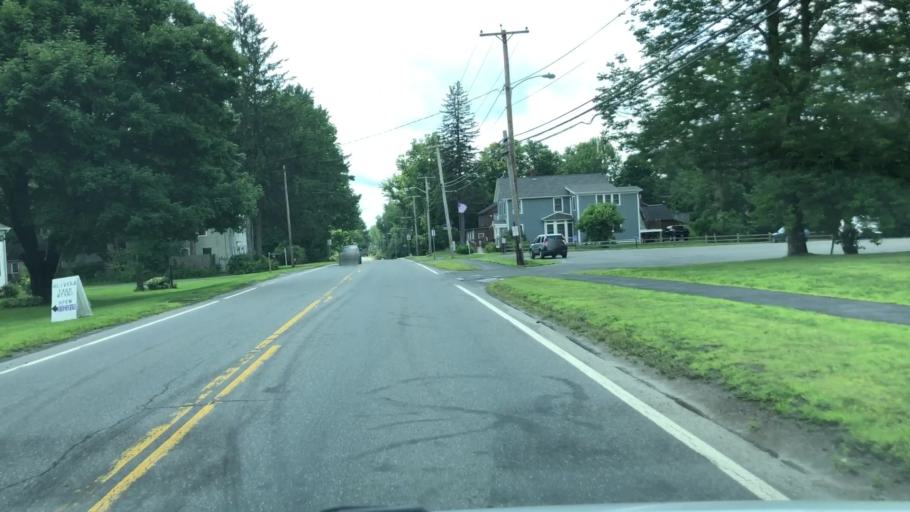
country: US
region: Massachusetts
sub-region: Hampshire County
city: Chesterfield
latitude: 42.4410
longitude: -72.8000
